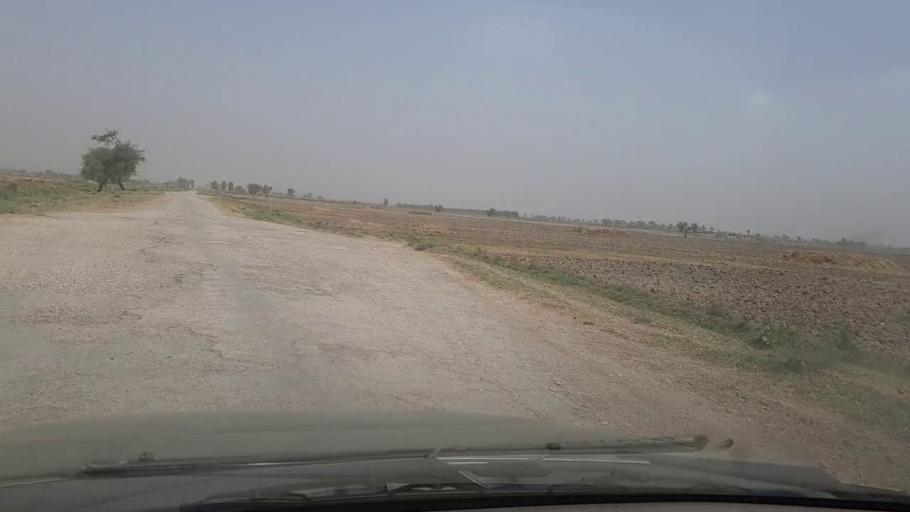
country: PK
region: Sindh
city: Madeji
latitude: 27.8108
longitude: 68.3978
